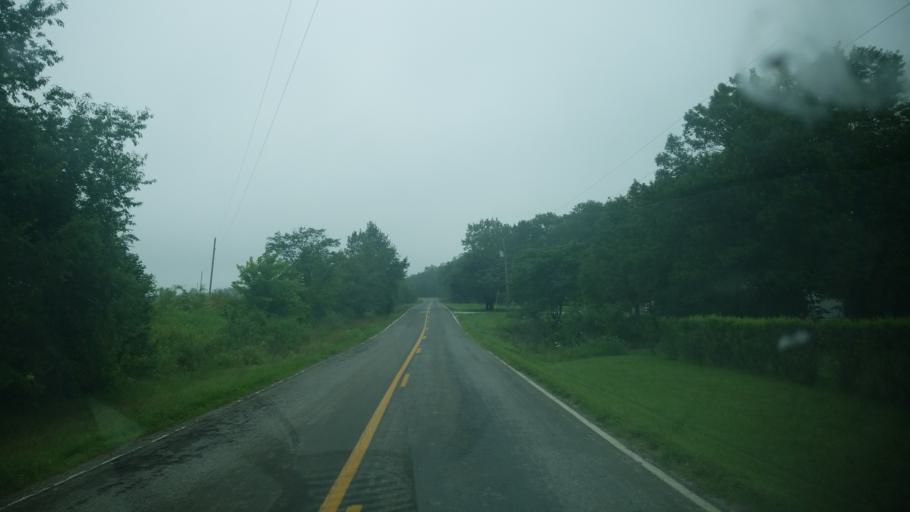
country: US
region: Missouri
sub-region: Audrain County
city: Vandalia
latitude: 39.3032
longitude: -91.3488
